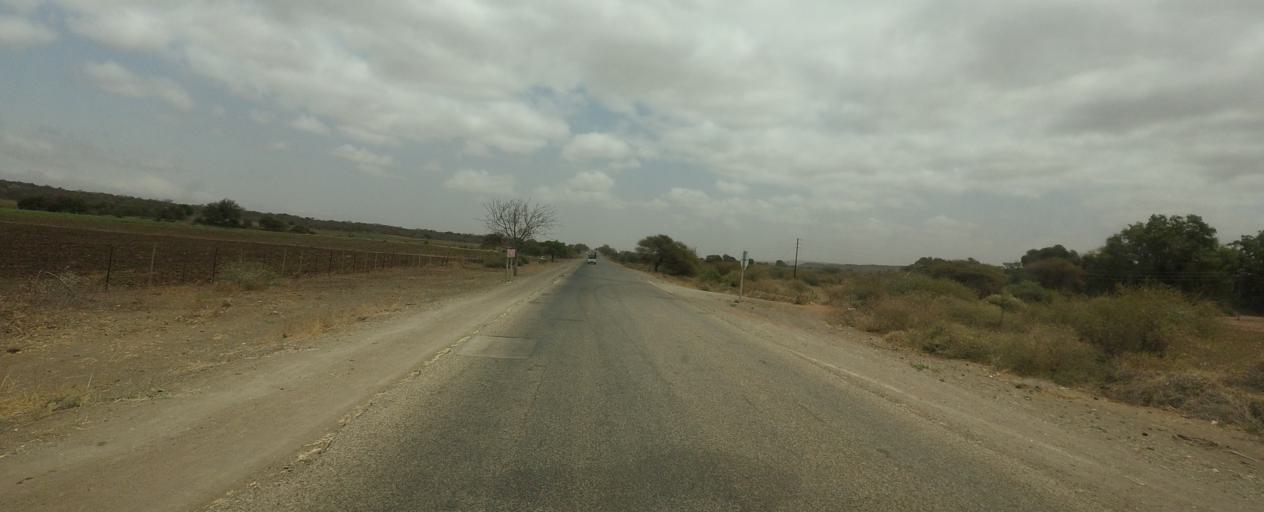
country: ZA
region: Limpopo
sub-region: Vhembe District Municipality
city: Mutale
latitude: -22.4472
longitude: 30.5121
